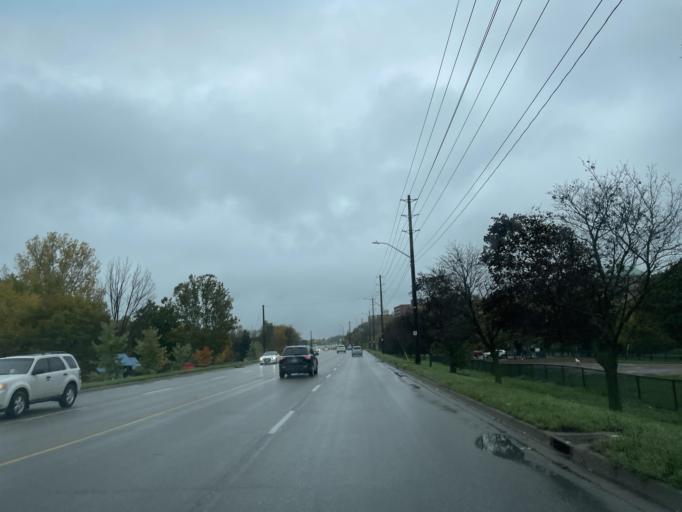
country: CA
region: Ontario
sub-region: Wellington County
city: Guelph
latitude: 43.5332
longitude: -80.2555
